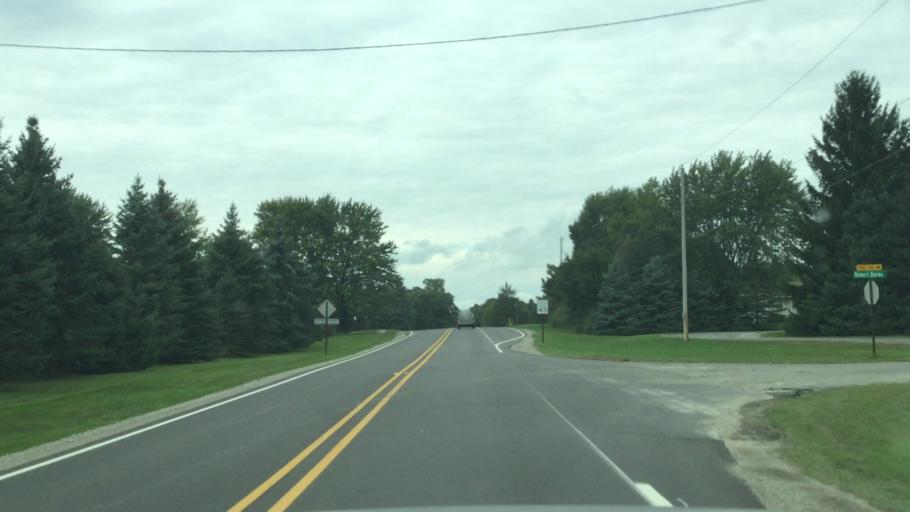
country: US
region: Michigan
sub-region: Livingston County
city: Whitmore Lake
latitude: 42.4674
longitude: -83.8057
